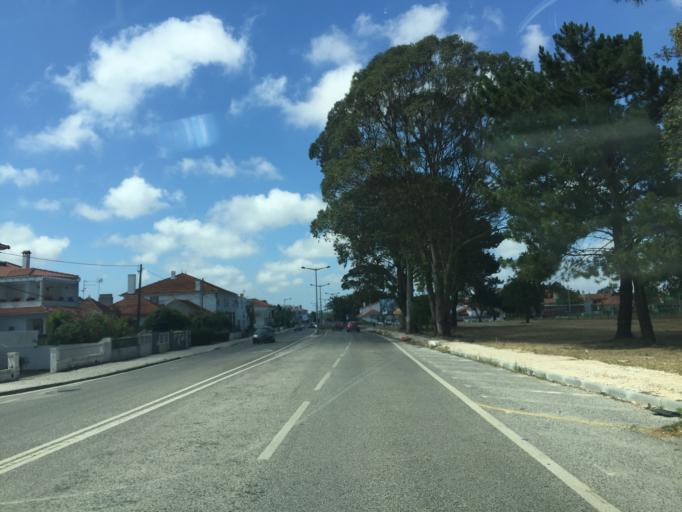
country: PT
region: Leiria
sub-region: Marinha Grande
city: Marinha Grande
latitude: 39.7393
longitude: -8.9341
